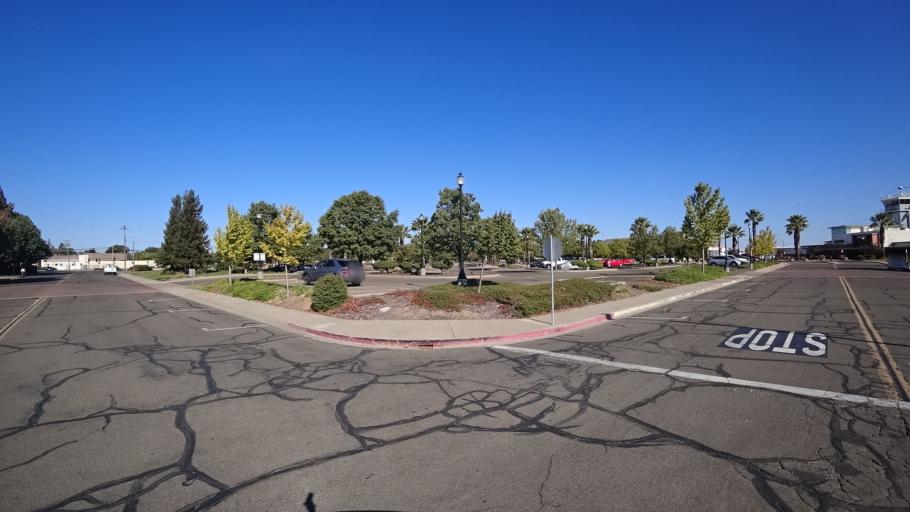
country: US
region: California
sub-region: Sacramento County
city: Parkway
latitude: 38.5127
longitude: -121.4994
